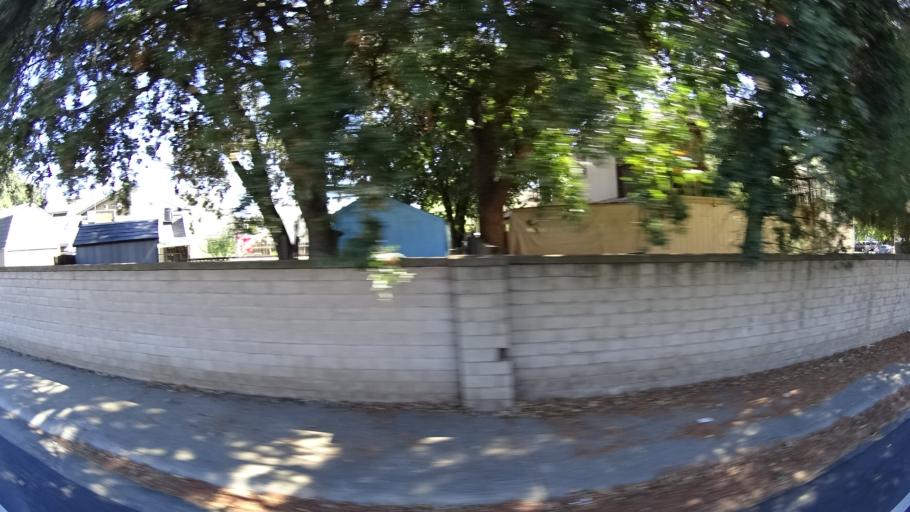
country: US
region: California
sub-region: Sacramento County
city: Elk Grove
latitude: 38.4184
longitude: -121.3715
